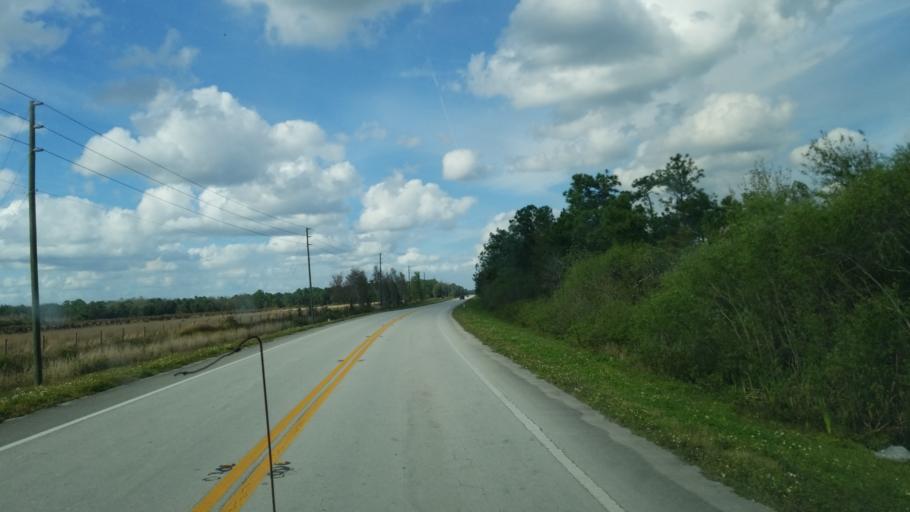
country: US
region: Florida
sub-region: Osceola County
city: Saint Cloud
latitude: 28.0734
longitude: -81.0684
